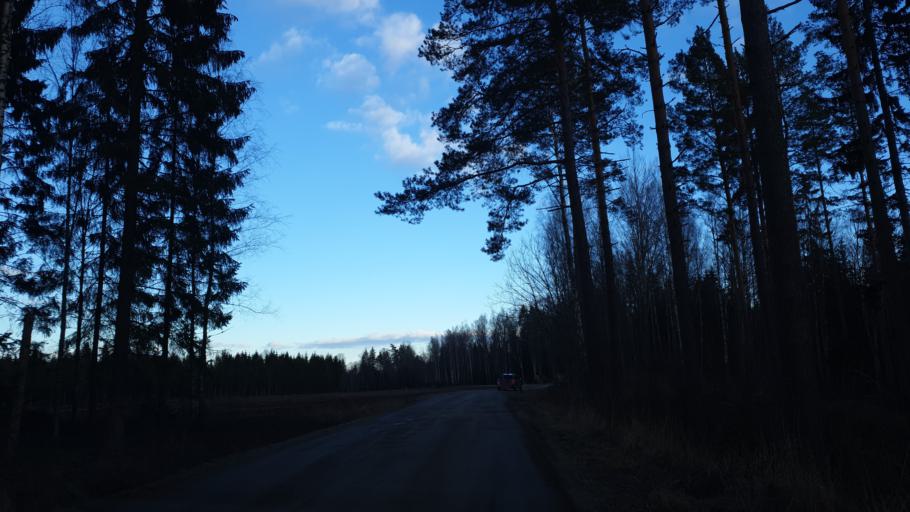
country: SE
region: OErebro
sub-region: Orebro Kommun
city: Garphyttan
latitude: 59.3494
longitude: 14.9911
